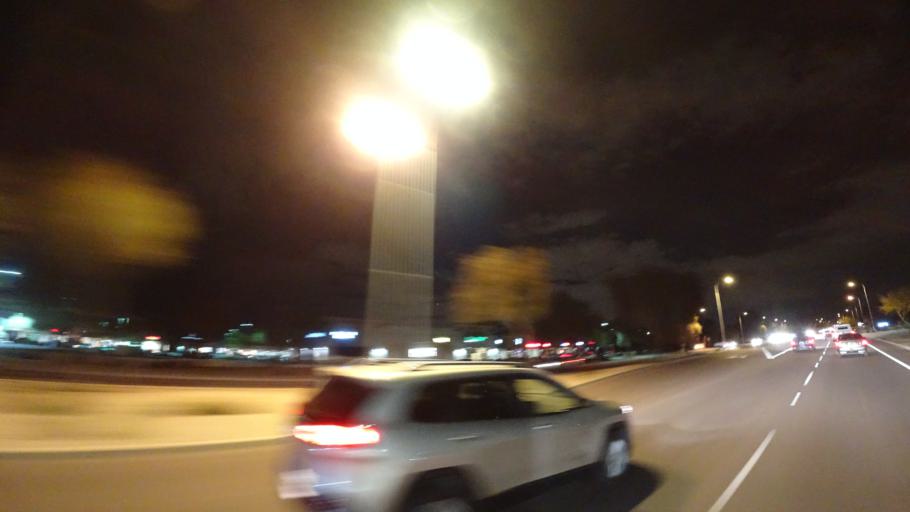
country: US
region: Arizona
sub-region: Maricopa County
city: Chandler
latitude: 33.2775
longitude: -111.8586
